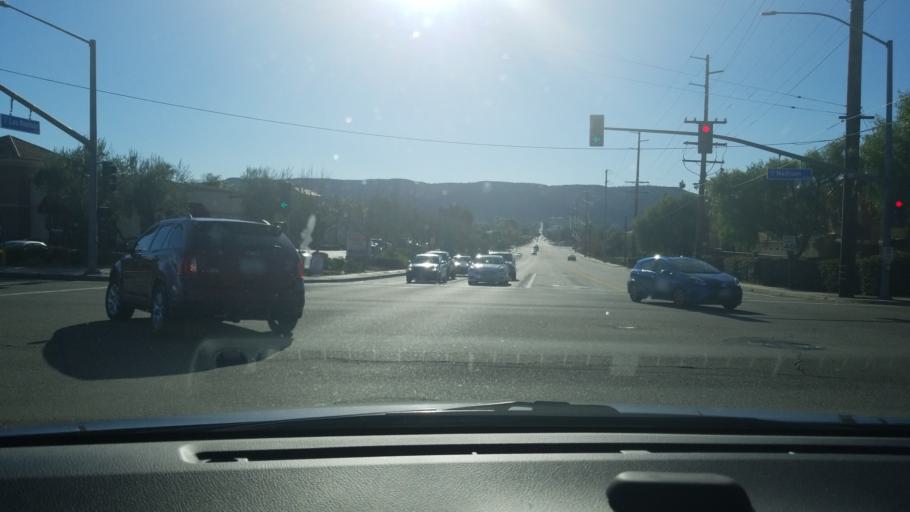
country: US
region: California
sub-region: Riverside County
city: Murrieta
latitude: 33.5585
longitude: -117.2015
